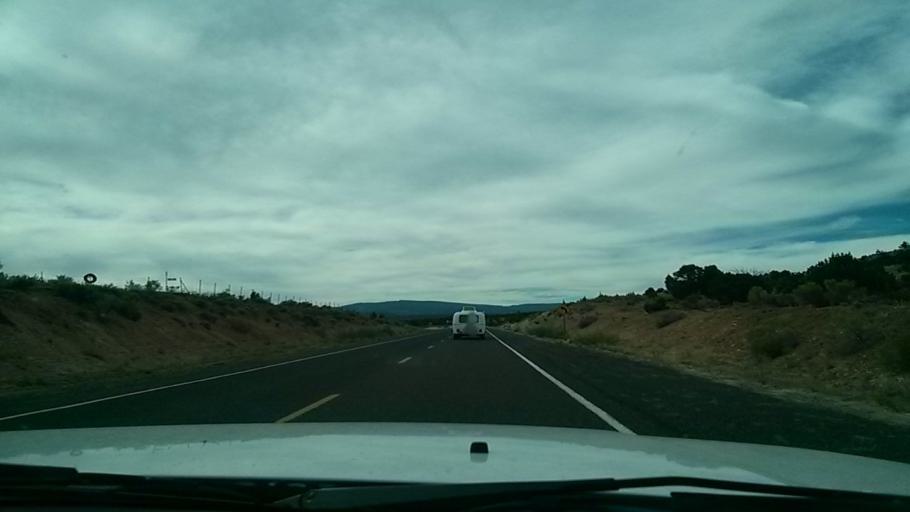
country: US
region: Utah
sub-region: Wayne County
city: Loa
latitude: 37.7527
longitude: -111.5680
